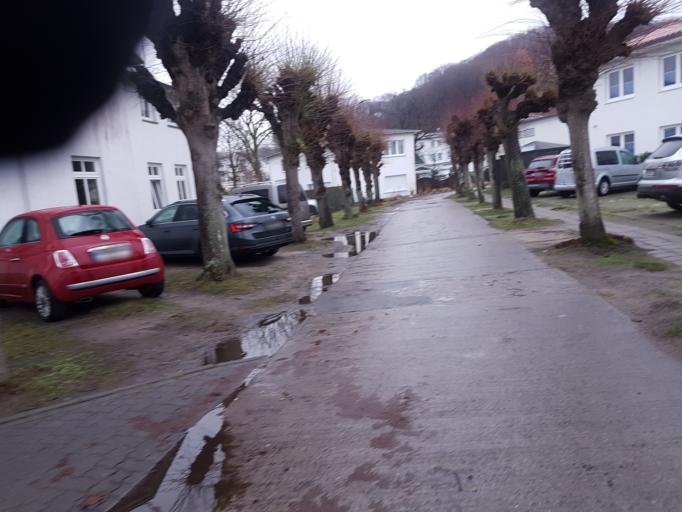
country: DE
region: Mecklenburg-Vorpommern
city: Ostseebad Binz
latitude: 54.3996
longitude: 13.6085
